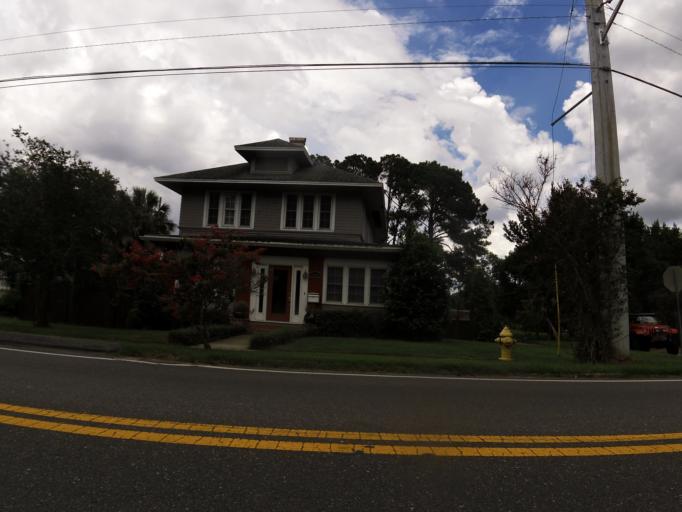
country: US
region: Florida
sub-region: Duval County
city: Jacksonville
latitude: 30.2920
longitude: -81.7102
